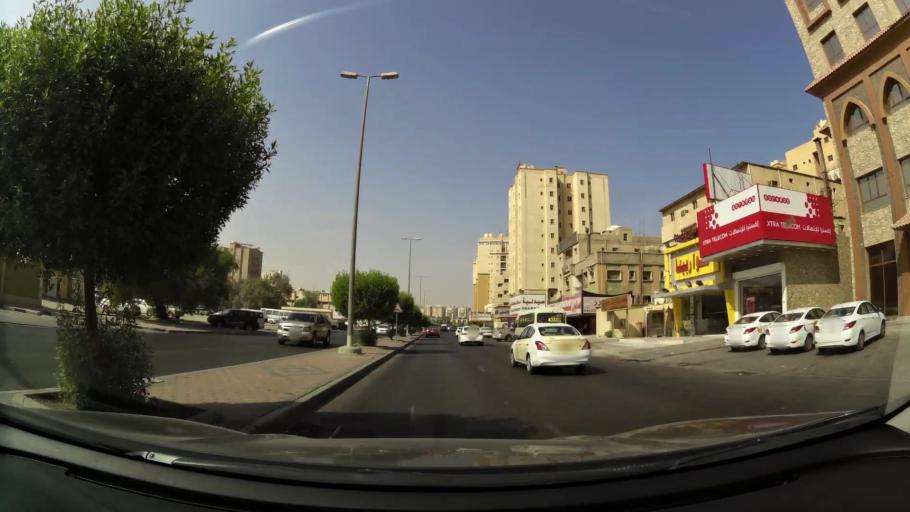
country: KW
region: Al Ahmadi
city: Al Fahahil
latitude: 29.0853
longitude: 48.1323
